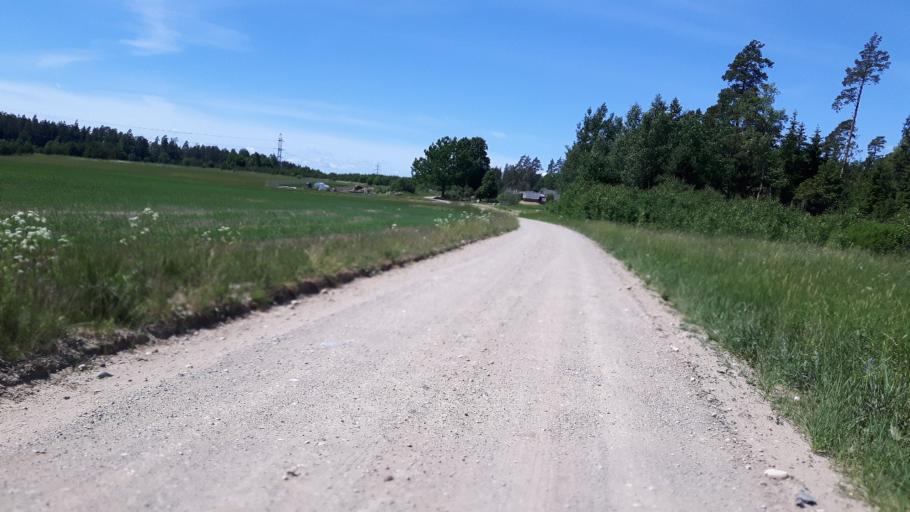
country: LV
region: Kandava
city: Kandava
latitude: 57.0406
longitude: 22.8240
